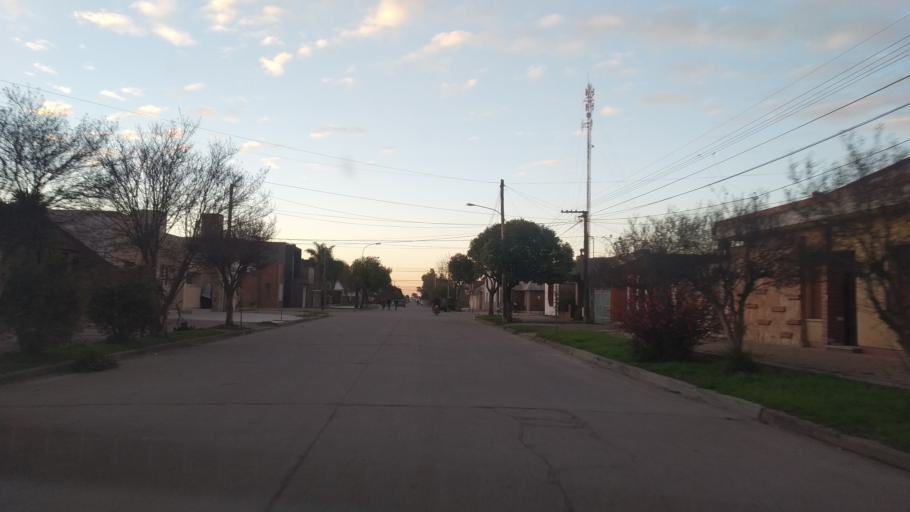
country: AR
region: Cordoba
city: Leones
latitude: -32.6303
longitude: -62.4784
